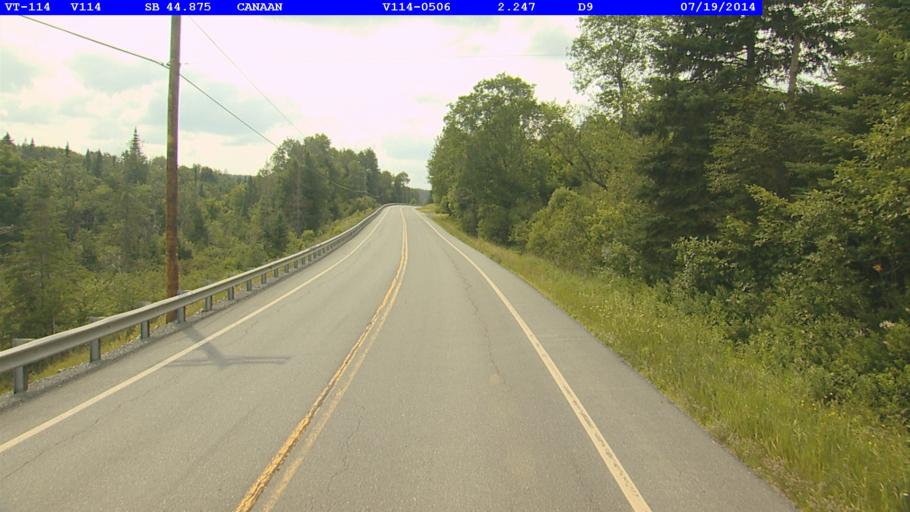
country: US
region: New Hampshire
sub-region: Coos County
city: Colebrook
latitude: 45.0061
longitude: -71.6482
